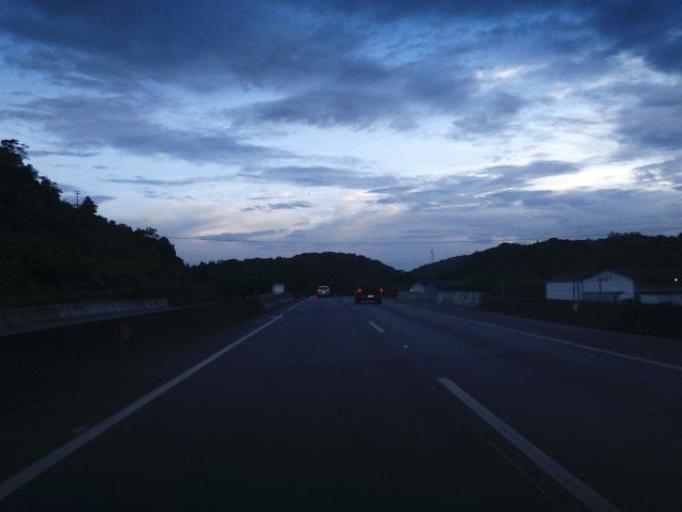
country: BR
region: Santa Catarina
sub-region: Joinville
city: Joinville
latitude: -26.2306
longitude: -48.9167
